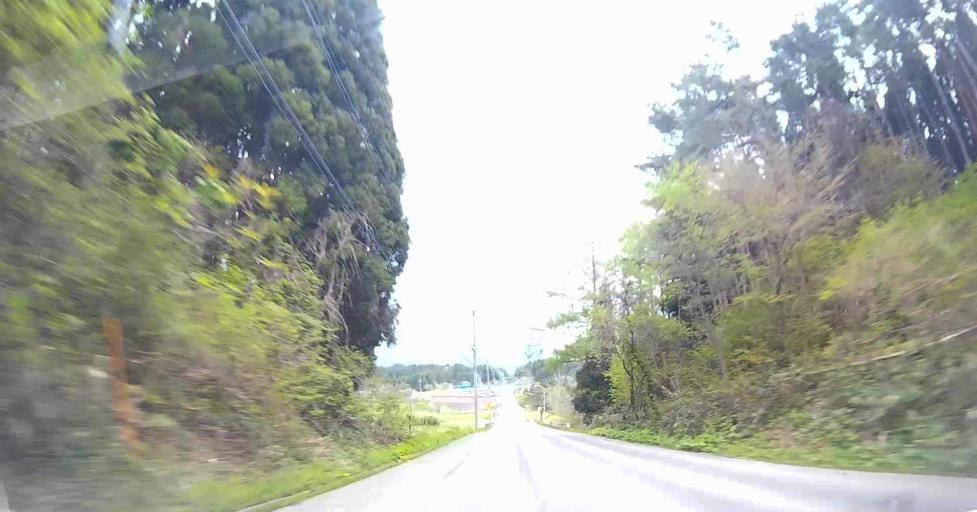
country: JP
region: Aomori
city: Goshogawara
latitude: 41.1782
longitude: 140.4747
